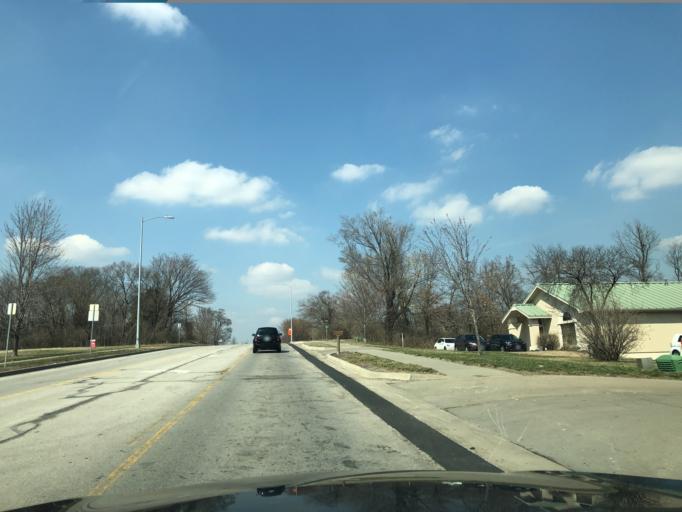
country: US
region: Missouri
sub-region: Platte County
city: Riverside
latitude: 39.1803
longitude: -94.6133
